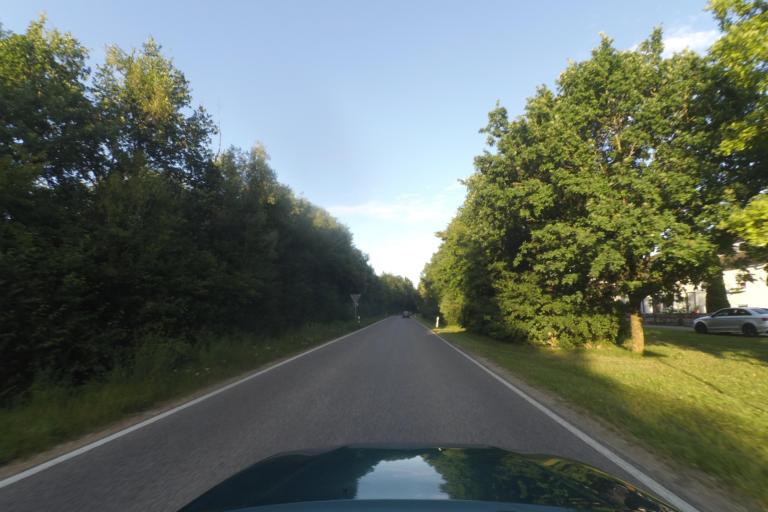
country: DE
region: Bavaria
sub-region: Upper Palatinate
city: Berching
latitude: 49.0400
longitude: 11.4839
